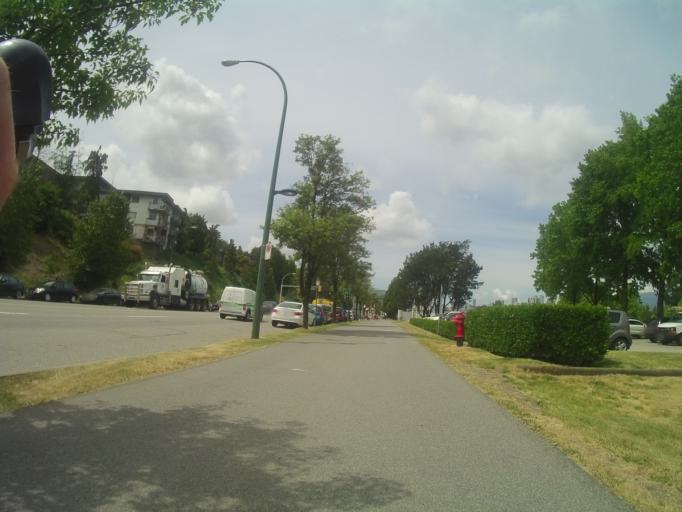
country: CA
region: British Columbia
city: Vancouver
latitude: 49.2661
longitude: -123.0851
